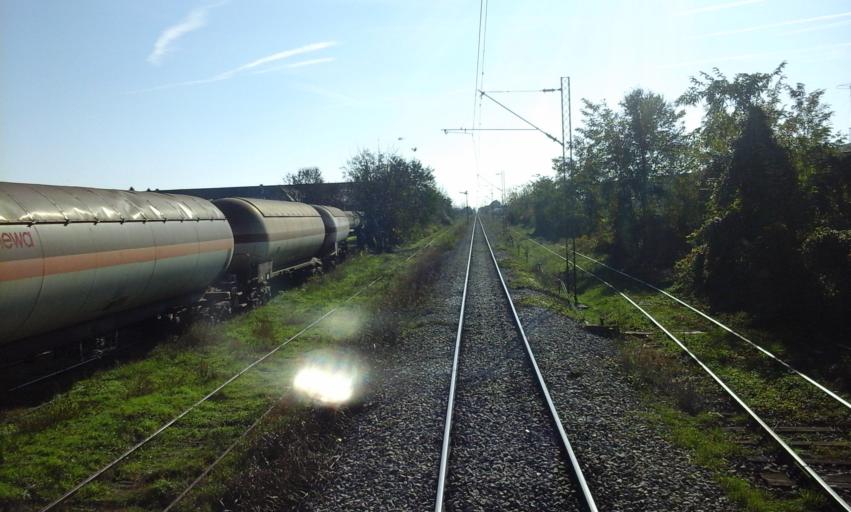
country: RS
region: Autonomna Pokrajina Vojvodina
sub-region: Severnobacki Okrug
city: Subotica
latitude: 46.0651
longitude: 19.6876
